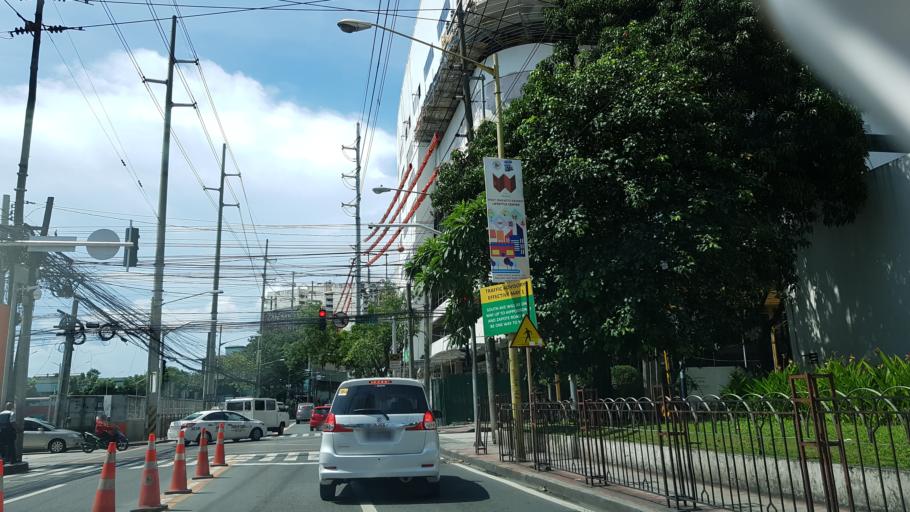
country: PH
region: Metro Manila
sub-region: Makati City
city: Makati City
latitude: 14.5602
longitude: 121.0116
